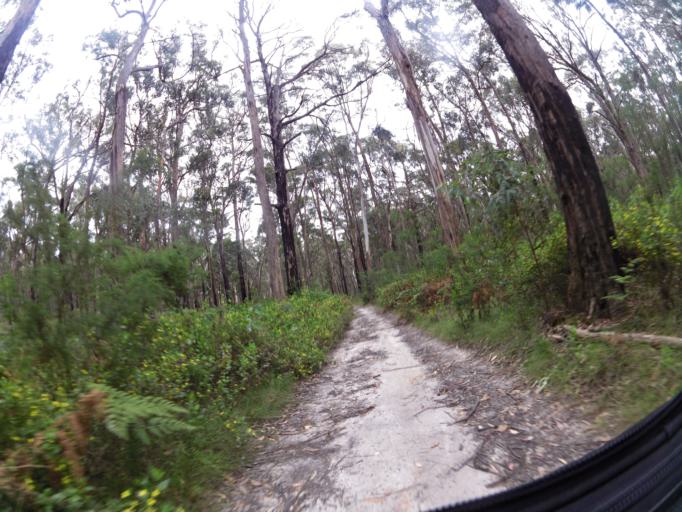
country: AU
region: Victoria
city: Brown Hill
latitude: -37.4928
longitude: 143.9080
